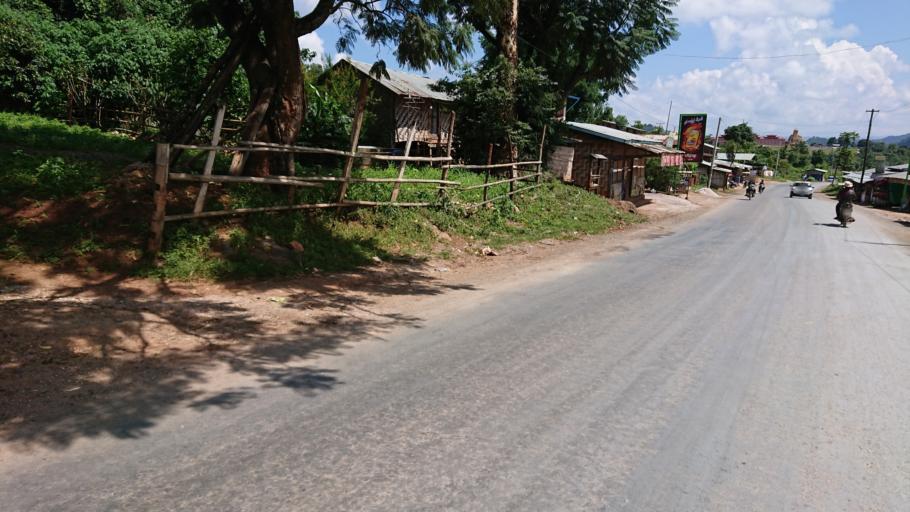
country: MM
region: Shan
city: Taunggyi
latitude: 20.8126
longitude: 97.3241
